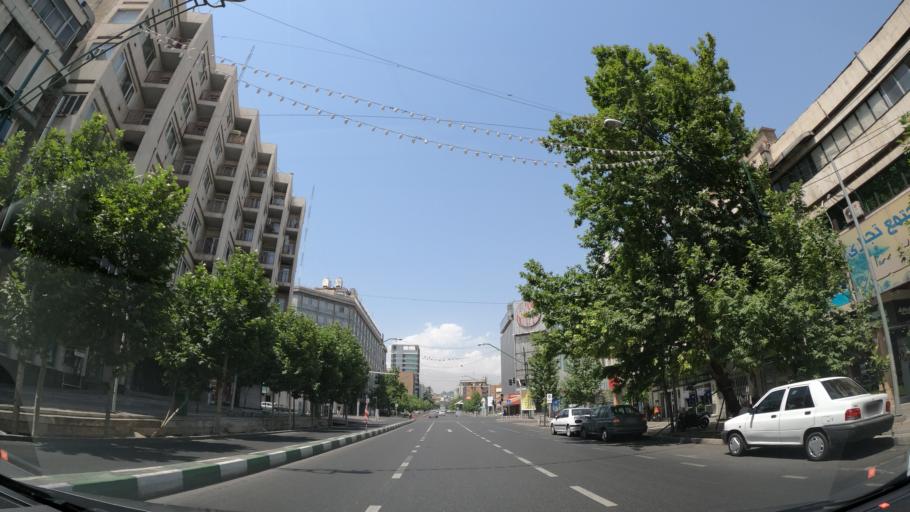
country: IR
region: Tehran
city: Tehran
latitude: 35.7202
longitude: 51.4136
